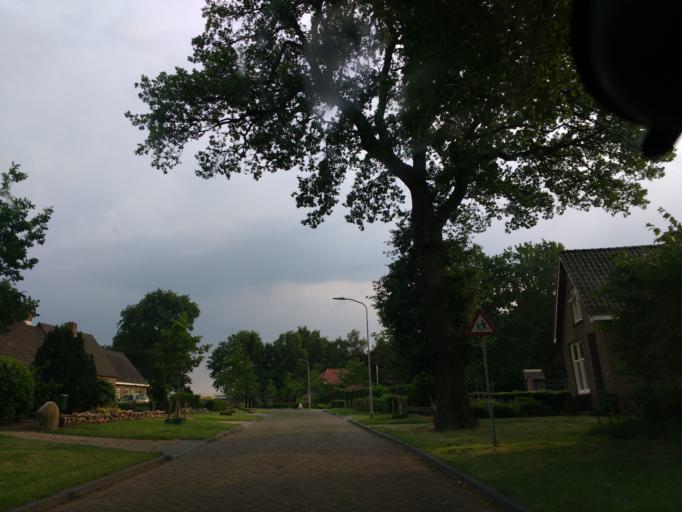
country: NL
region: Drenthe
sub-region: Gemeente Borger-Odoorn
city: Borger
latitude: 52.9072
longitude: 6.8045
